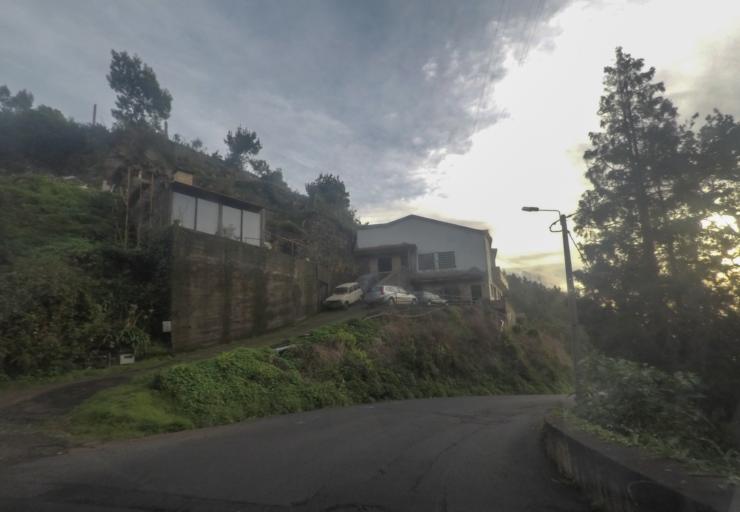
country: PT
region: Madeira
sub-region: Funchal
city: Nossa Senhora do Monte
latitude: 32.6598
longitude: -16.8725
